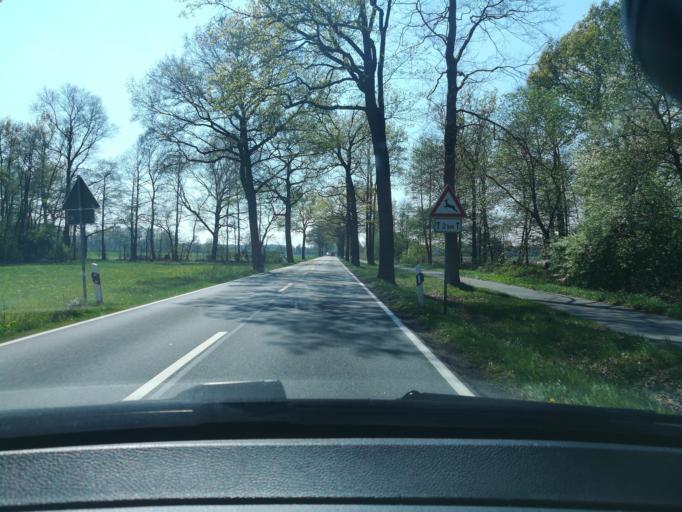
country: DE
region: North Rhine-Westphalia
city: Borgholzhausen
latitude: 52.0347
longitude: 8.2678
